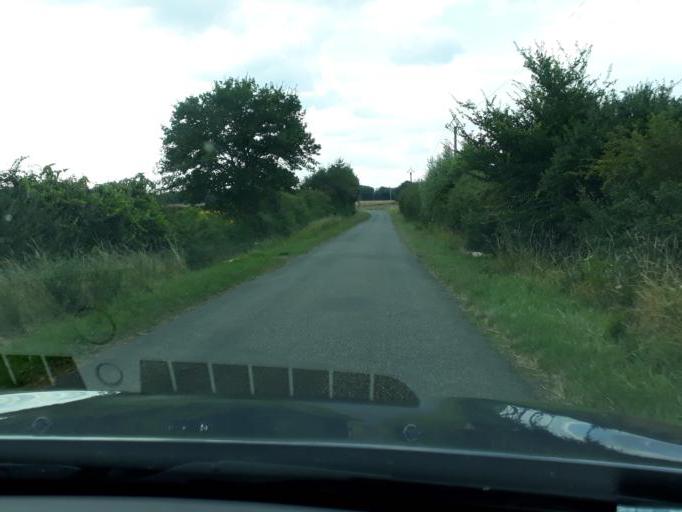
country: FR
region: Centre
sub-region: Departement du Cher
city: Jouet-sur-l'Aubois
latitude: 46.9843
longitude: 2.9246
